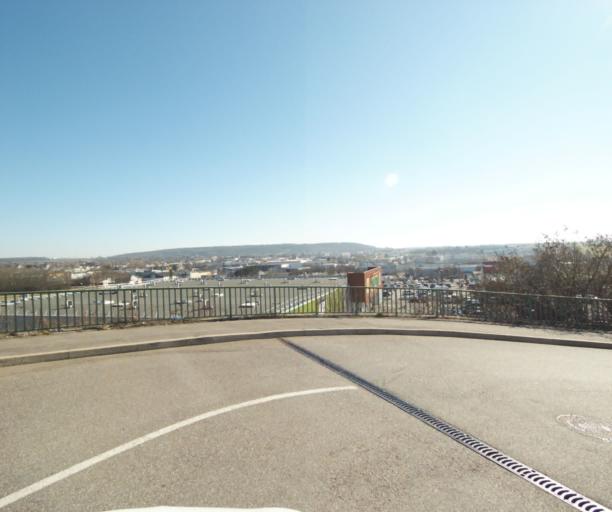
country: FR
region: Lorraine
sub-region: Departement de Meurthe-et-Moselle
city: Pulnoy
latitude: 48.7125
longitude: 6.2410
